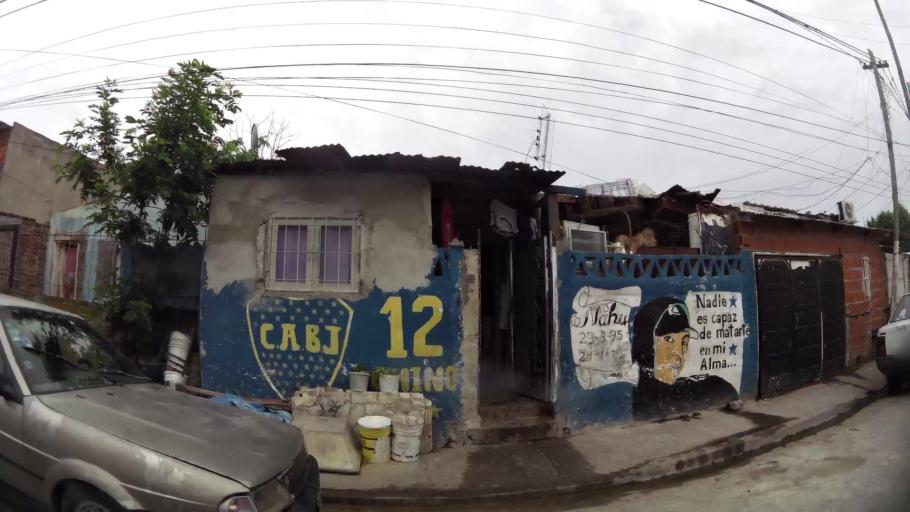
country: AR
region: Buenos Aires
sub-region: Partido de Avellaneda
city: Avellaneda
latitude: -34.6533
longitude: -58.3605
